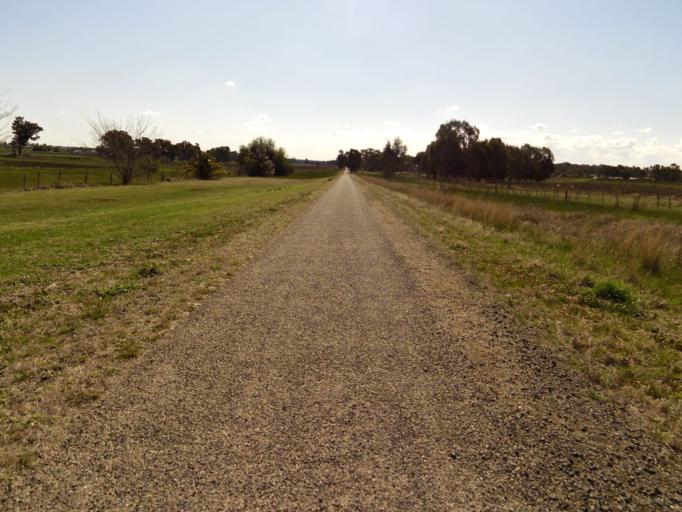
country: AU
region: New South Wales
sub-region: Corowa Shire
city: Corowa
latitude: -36.0501
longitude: 146.4601
